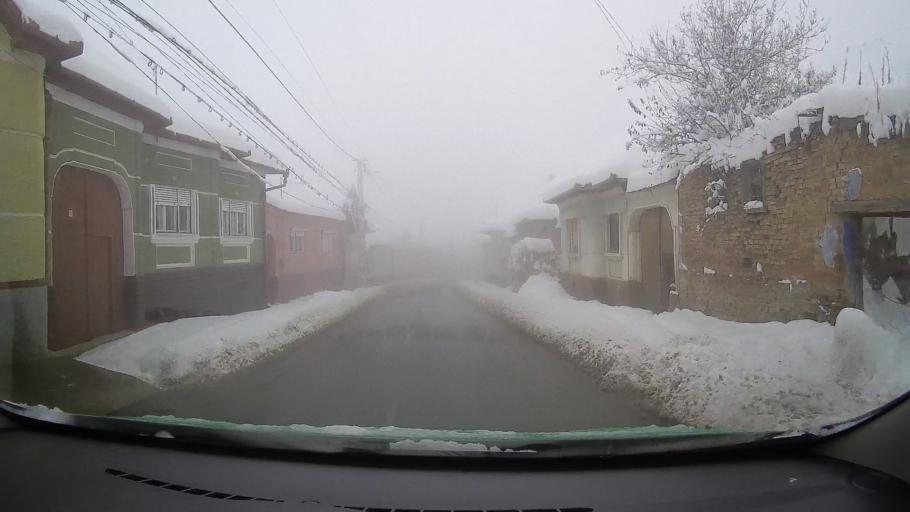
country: RO
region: Sibiu
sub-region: Comuna Poiana Sibiului
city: Poiana Sibiului
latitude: 45.8018
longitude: 23.7181
